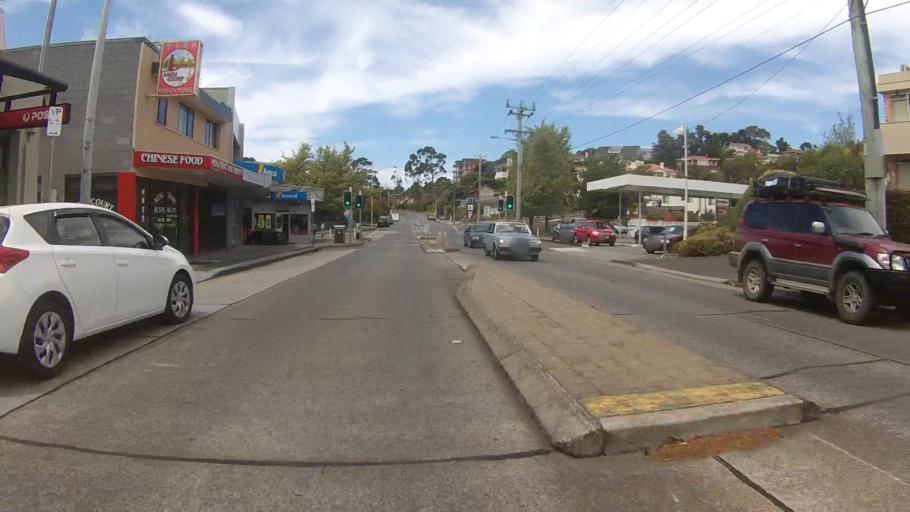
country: AU
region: Tasmania
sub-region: Kingborough
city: Taroona
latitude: -42.9129
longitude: 147.3547
